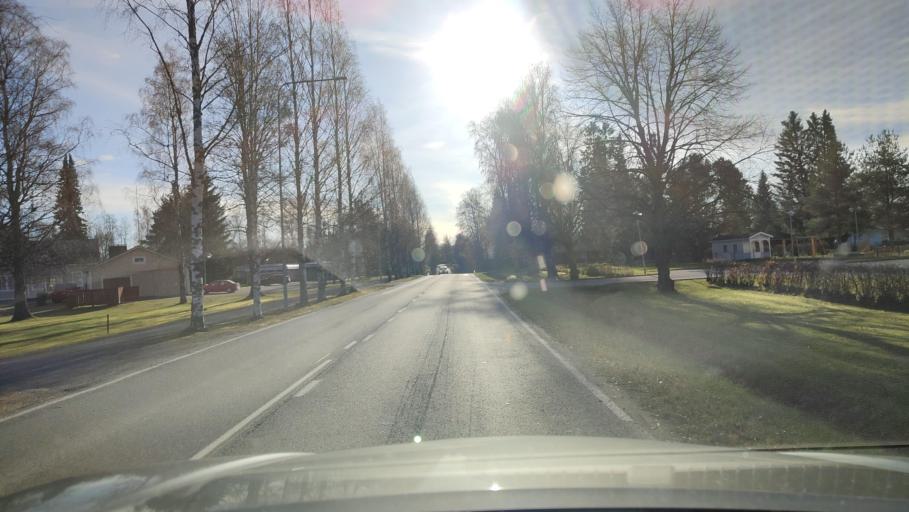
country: FI
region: Southern Ostrobothnia
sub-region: Suupohja
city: Teuva
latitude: 62.4791
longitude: 21.7393
